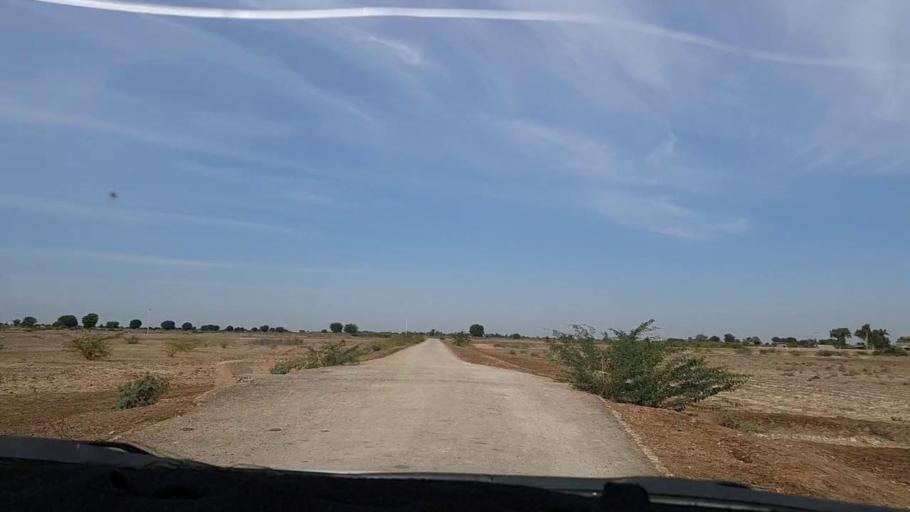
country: PK
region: Sindh
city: Pithoro
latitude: 25.4709
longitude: 69.4704
